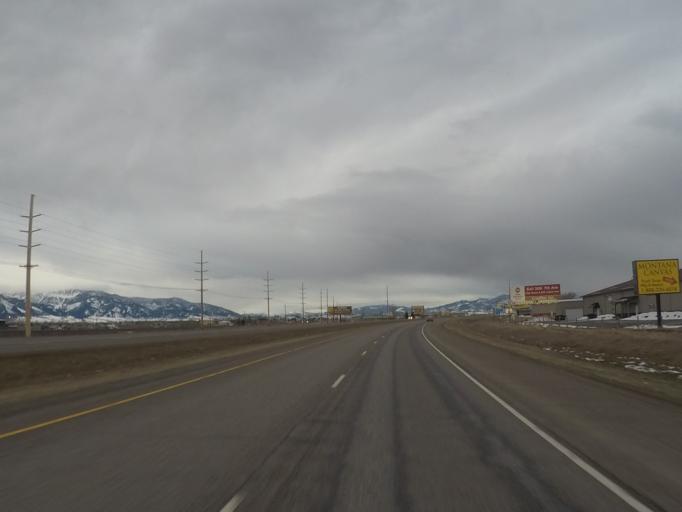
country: US
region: Montana
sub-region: Gallatin County
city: Belgrade
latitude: 45.7902
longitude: -111.2072
